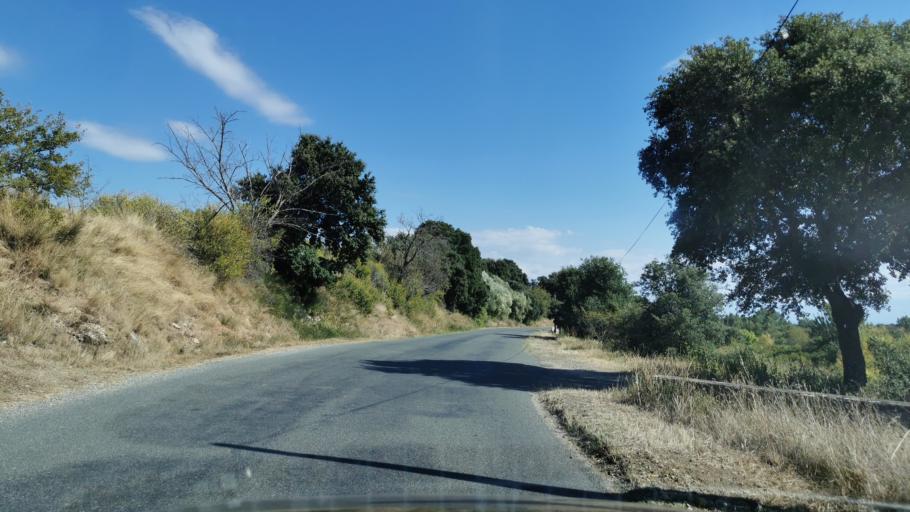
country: FR
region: Languedoc-Roussillon
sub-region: Departement de l'Aude
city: Caunes-Minervois
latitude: 43.3158
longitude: 2.5480
